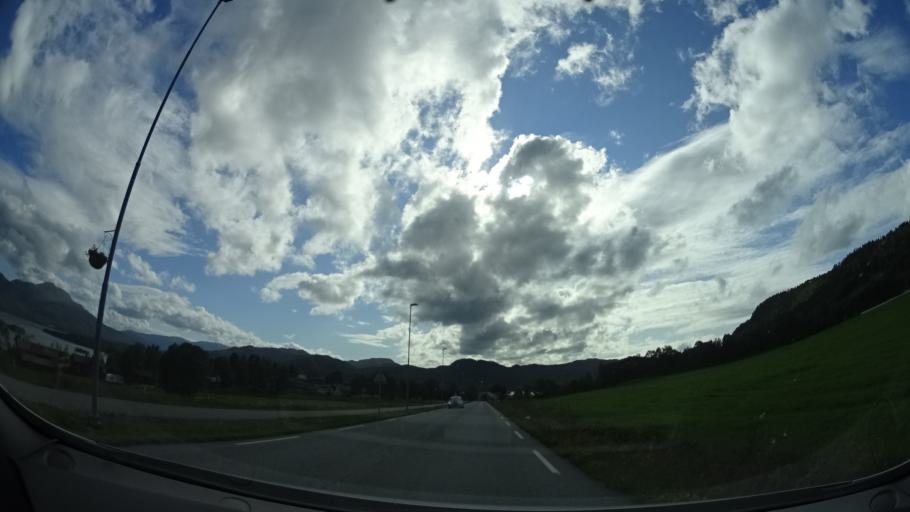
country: NO
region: More og Romsdal
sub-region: Halsa
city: Liaboen
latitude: 63.1210
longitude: 8.3176
